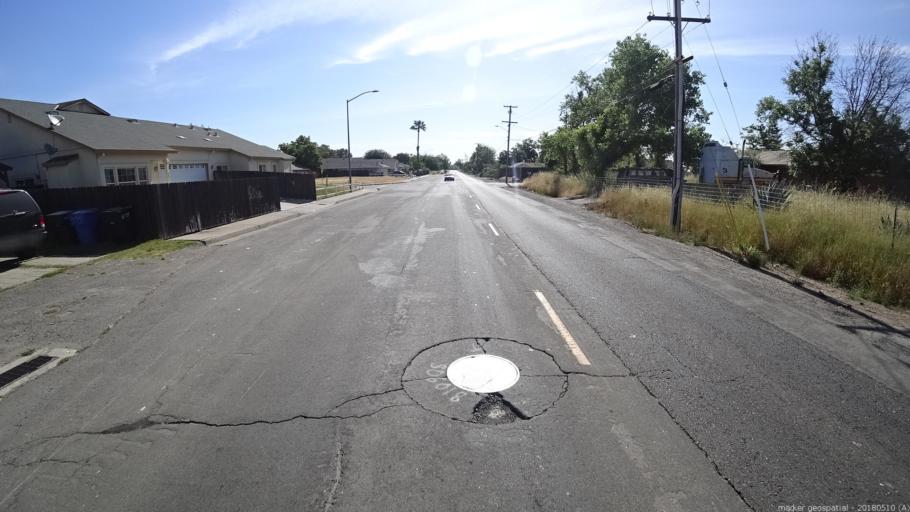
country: US
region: California
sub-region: Sacramento County
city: Rio Linda
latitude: 38.6549
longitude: -121.4529
